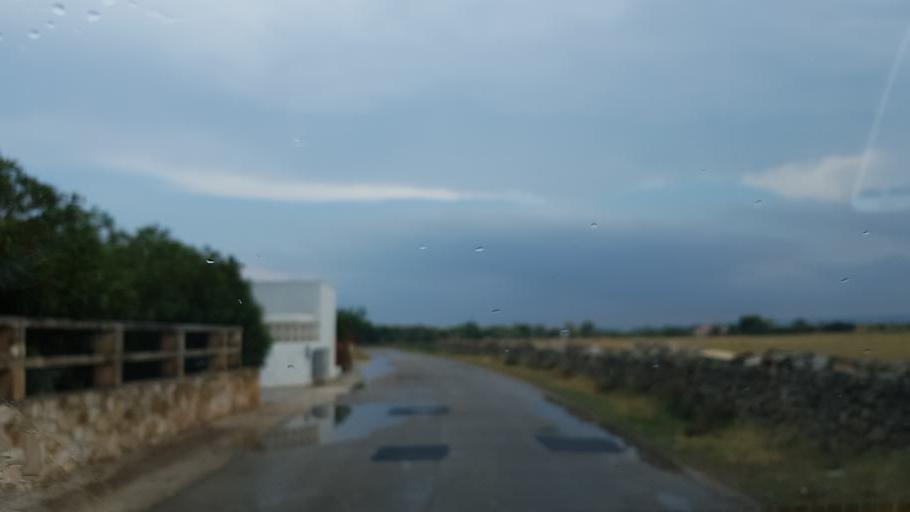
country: IT
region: Apulia
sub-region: Provincia di Bari
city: Monopoli
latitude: 40.9304
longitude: 17.3262
